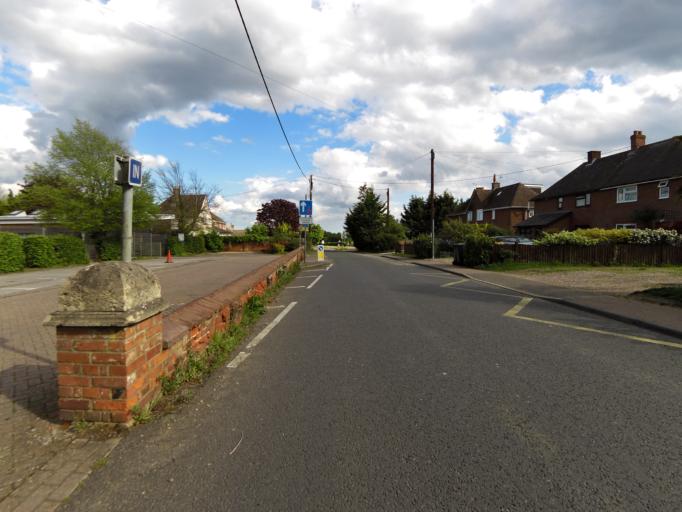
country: GB
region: England
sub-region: Suffolk
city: Woolpit
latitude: 52.2218
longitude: 0.8951
